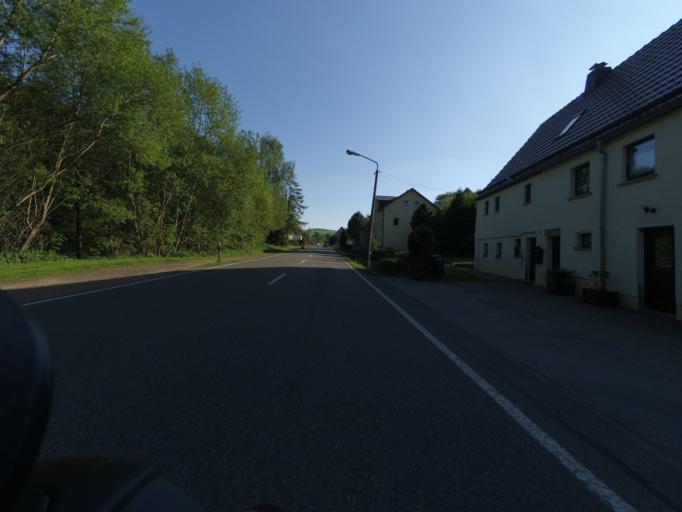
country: DE
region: Saxony
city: Dippoldiswalde
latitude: 50.8890
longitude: 13.6460
